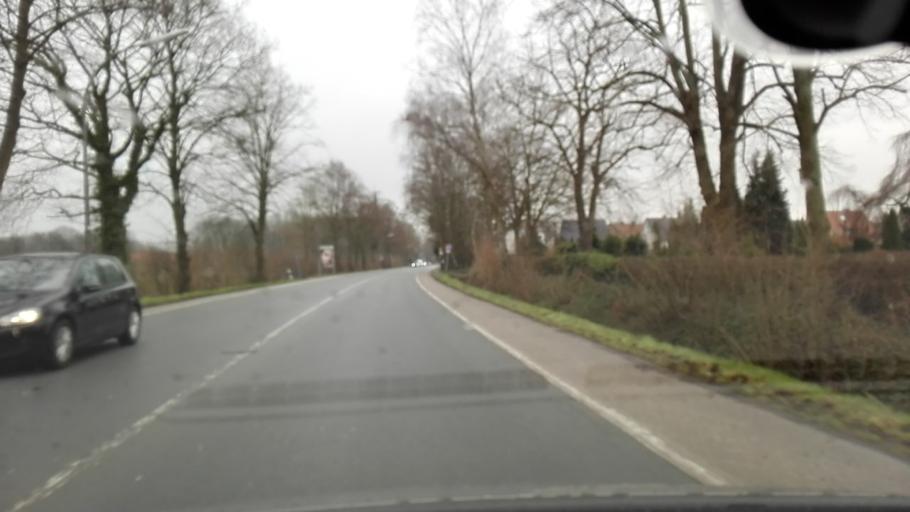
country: DE
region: North Rhine-Westphalia
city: Kamen
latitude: 51.5842
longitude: 7.7035
